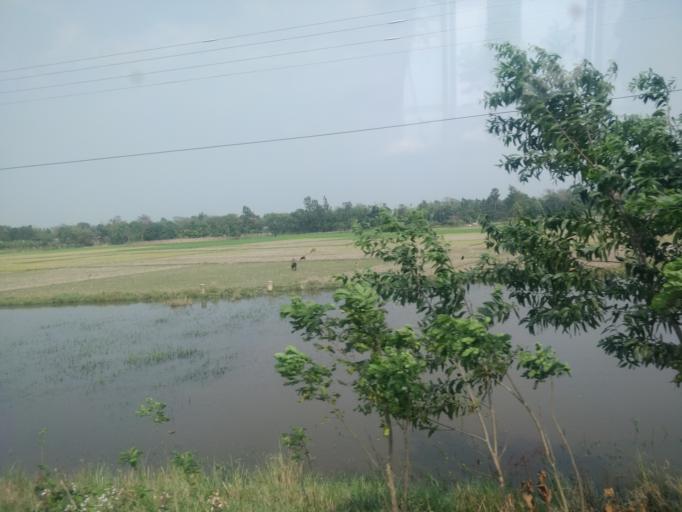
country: BD
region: Sylhet
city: Habiganj
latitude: 24.3201
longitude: 91.4350
